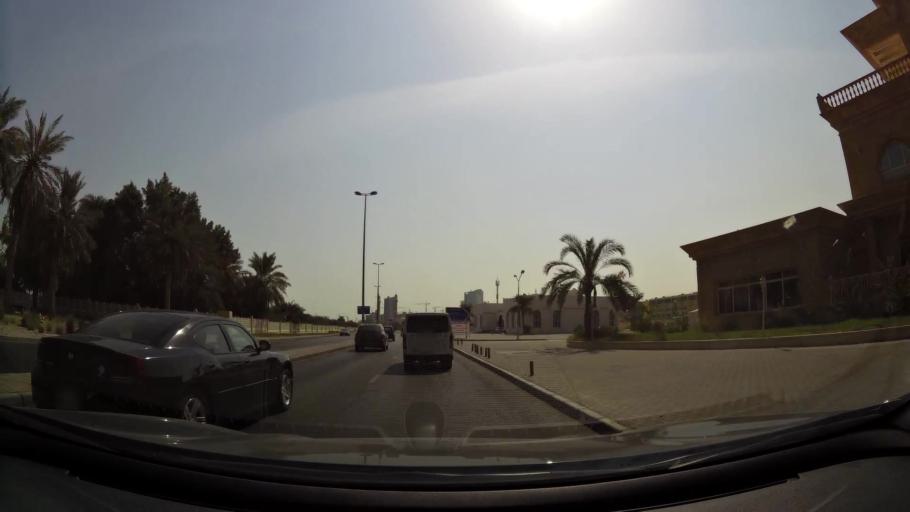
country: KW
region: Al Ahmadi
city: Al Manqaf
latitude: 29.0898
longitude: 48.1378
